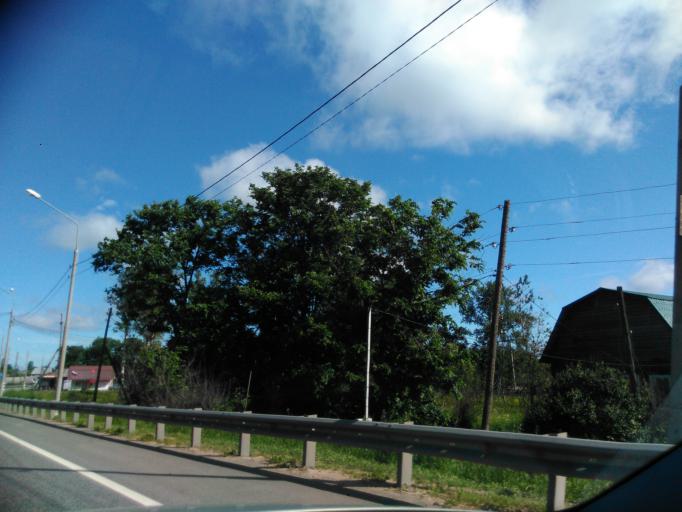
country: RU
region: Tverskaya
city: Zavidovo
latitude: 56.5191
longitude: 36.5323
